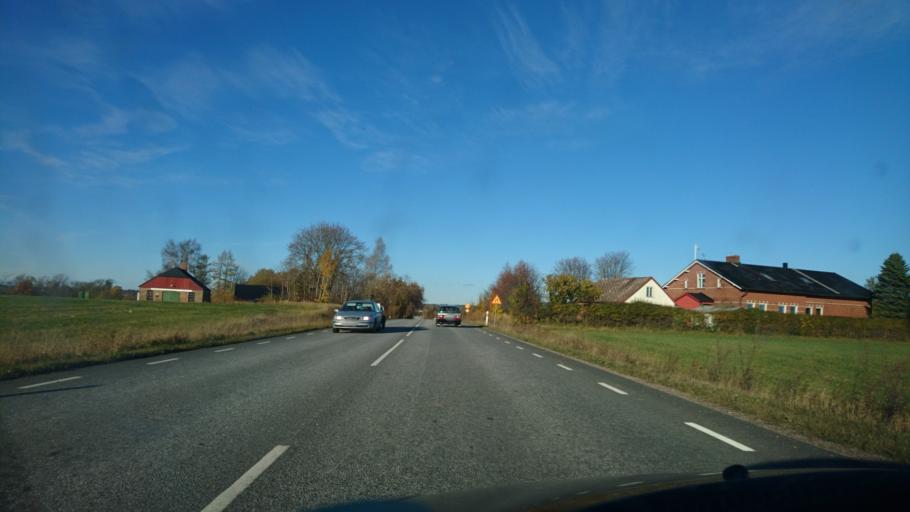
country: SE
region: Skane
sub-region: Tomelilla Kommun
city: Tomelilla
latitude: 55.5642
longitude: 13.9622
